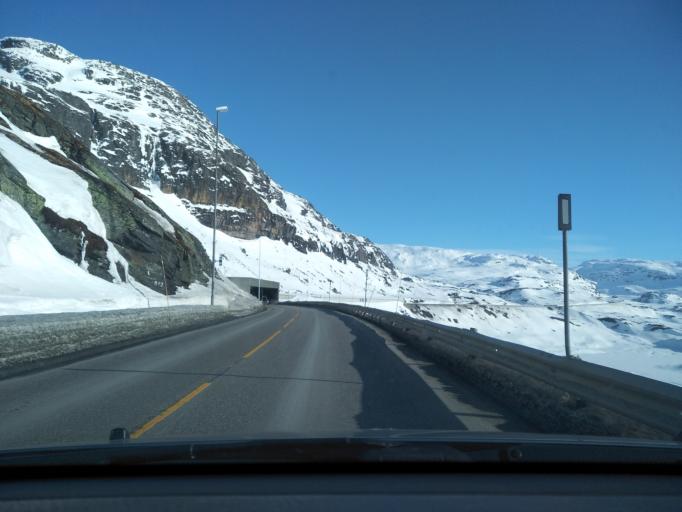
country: NO
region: Hordaland
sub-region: Odda
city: Odda
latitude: 59.8489
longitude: 6.9565
